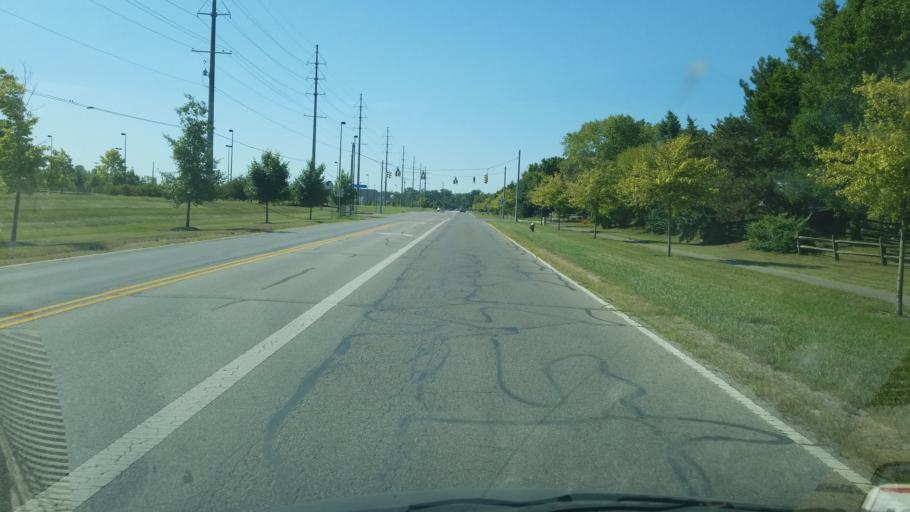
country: US
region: Ohio
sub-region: Franklin County
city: Hilliard
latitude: 40.0560
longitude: -83.1357
